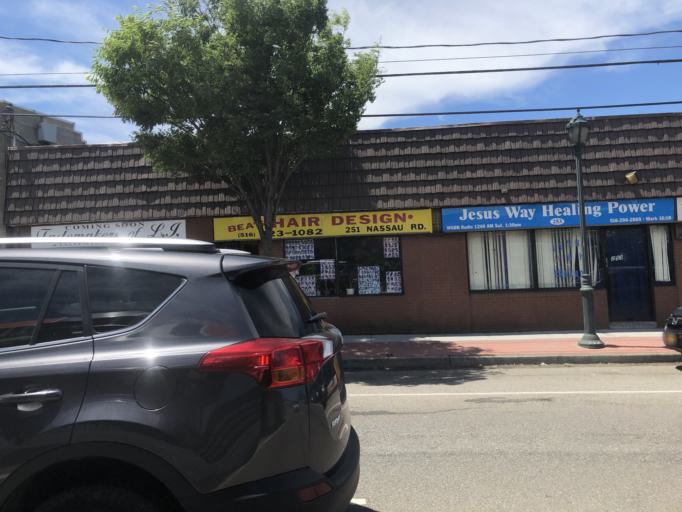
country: US
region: New York
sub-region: Nassau County
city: Roosevelt
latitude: 40.6788
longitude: -73.5894
